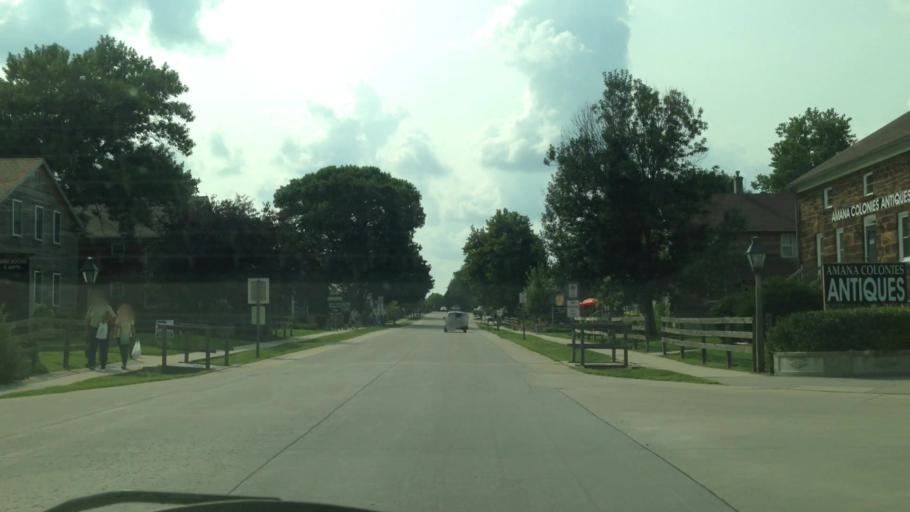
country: US
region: Iowa
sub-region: Benton County
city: Walford
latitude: 41.7997
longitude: -91.8683
